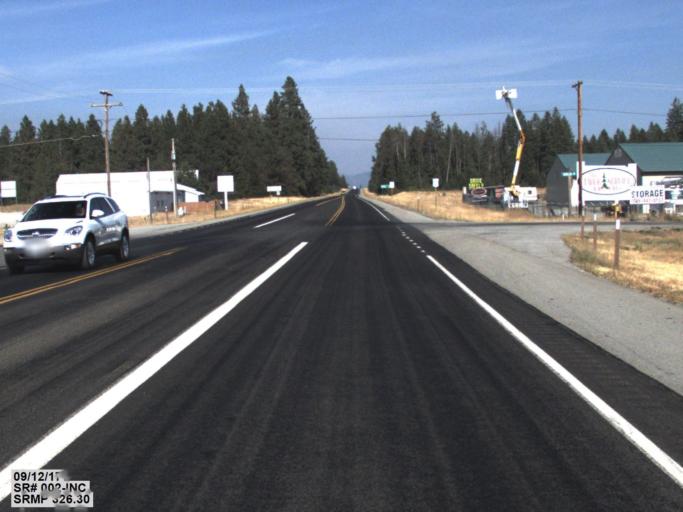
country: US
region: Washington
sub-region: Pend Oreille County
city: Newport
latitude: 48.1276
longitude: -117.1853
